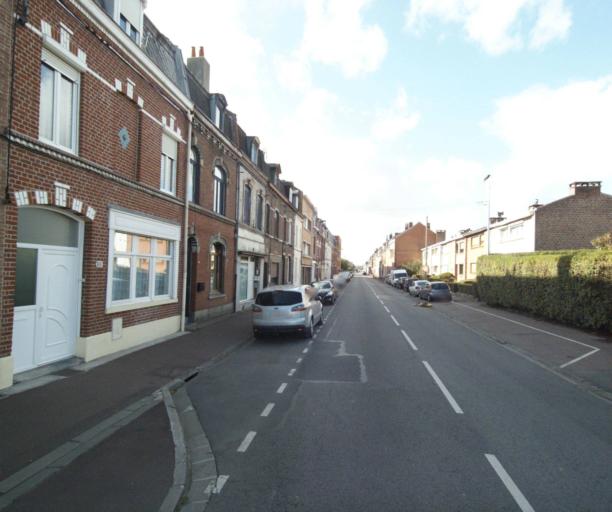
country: FR
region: Nord-Pas-de-Calais
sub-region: Departement du Nord
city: Loos
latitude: 50.6292
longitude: 3.0109
